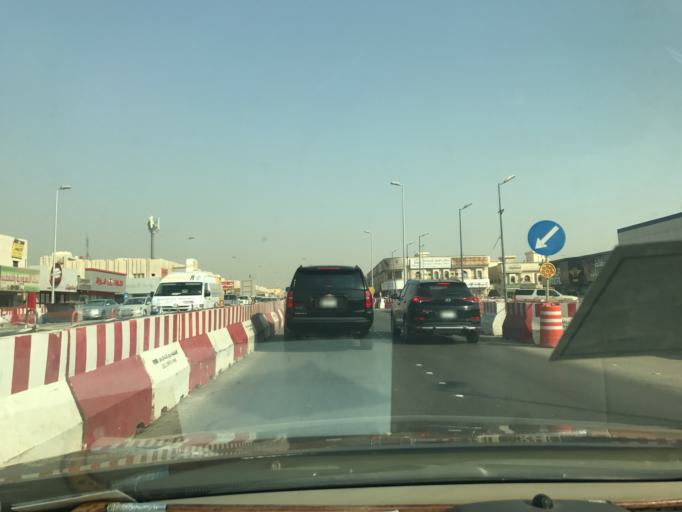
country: SA
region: Ar Riyad
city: Riyadh
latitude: 24.7535
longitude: 46.7699
